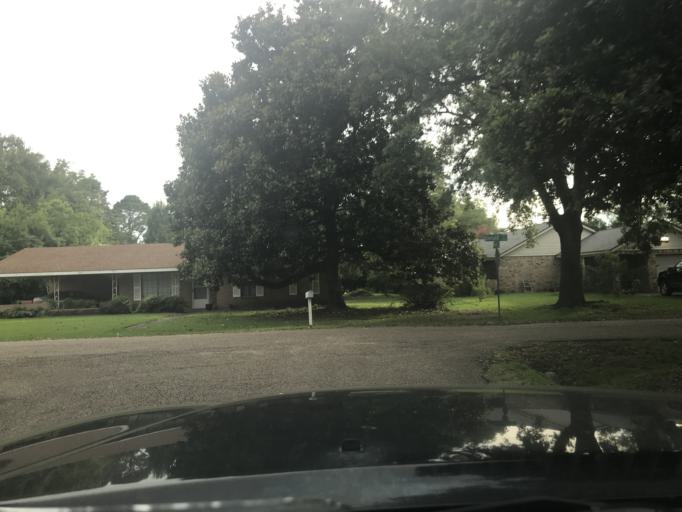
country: US
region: Louisiana
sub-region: Lafayette Parish
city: Lafayette
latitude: 30.2003
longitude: -92.0490
